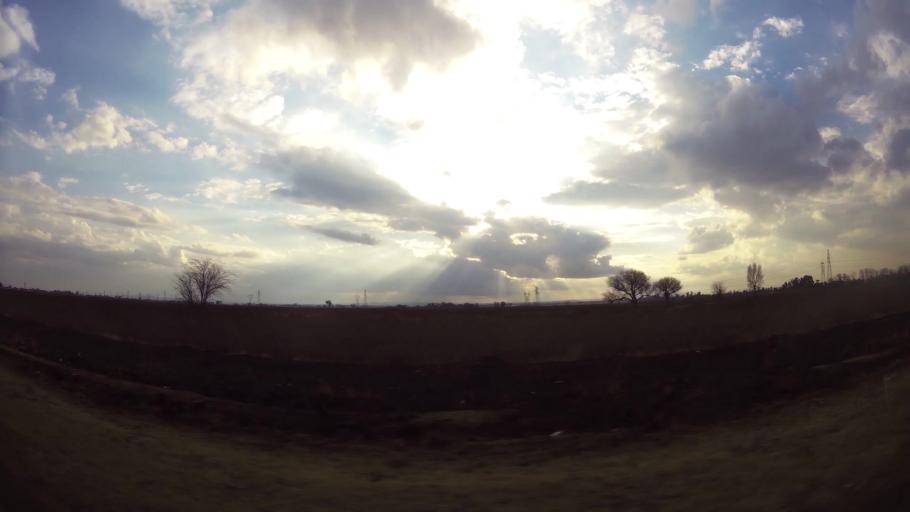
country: ZA
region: Gauteng
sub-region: Sedibeng District Municipality
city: Vanderbijlpark
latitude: -26.6670
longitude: 27.7955
